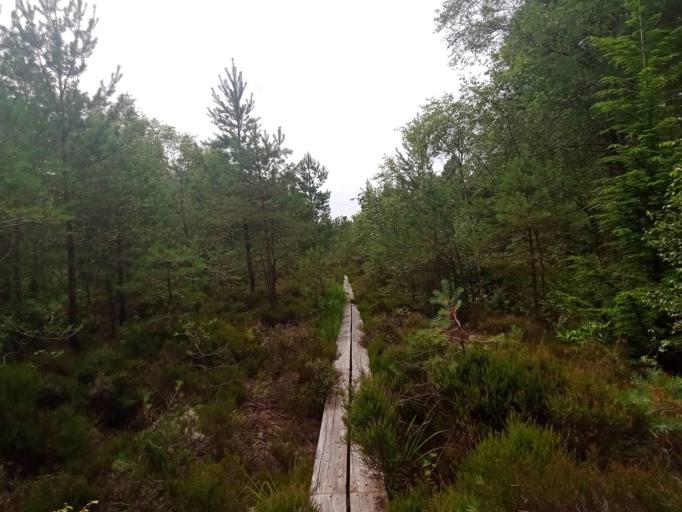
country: IE
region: Leinster
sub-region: Laois
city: Abbeyleix
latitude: 52.8885
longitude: -7.3595
